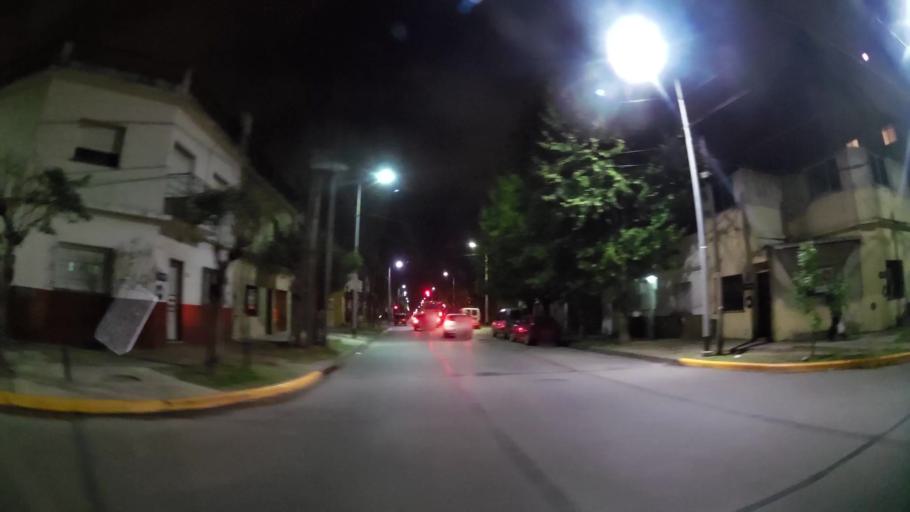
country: AR
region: Buenos Aires
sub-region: Partido de Avellaneda
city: Avellaneda
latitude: -34.7121
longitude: -58.3255
